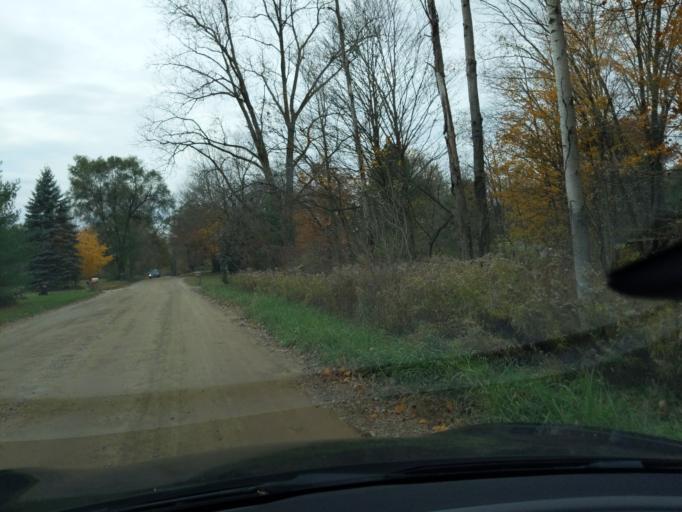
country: US
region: Michigan
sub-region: Eaton County
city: Eaton Rapids
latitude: 42.5531
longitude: -84.6102
